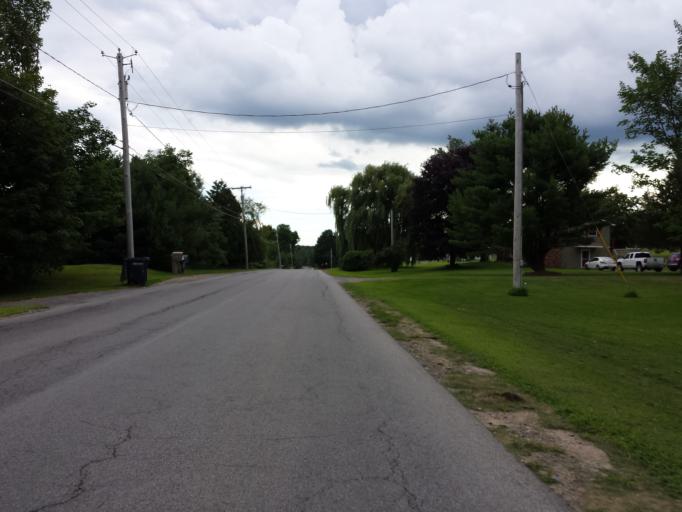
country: US
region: New York
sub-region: St. Lawrence County
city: Potsdam
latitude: 44.6951
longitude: -75.0131
